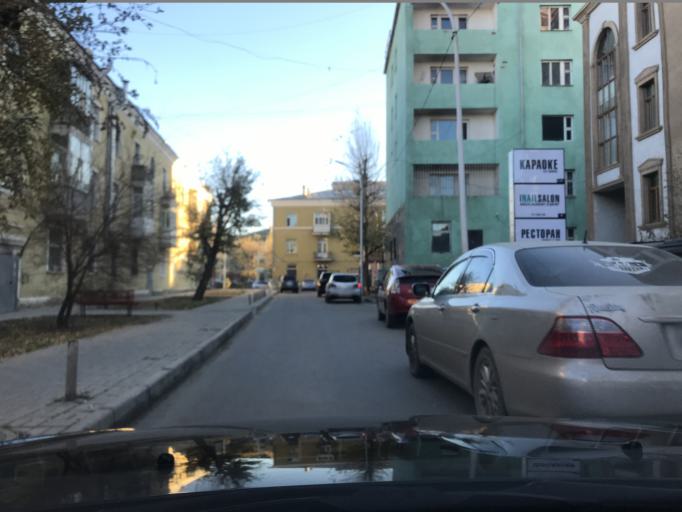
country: MN
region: Ulaanbaatar
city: Ulaanbaatar
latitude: 47.9233
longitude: 106.9101
